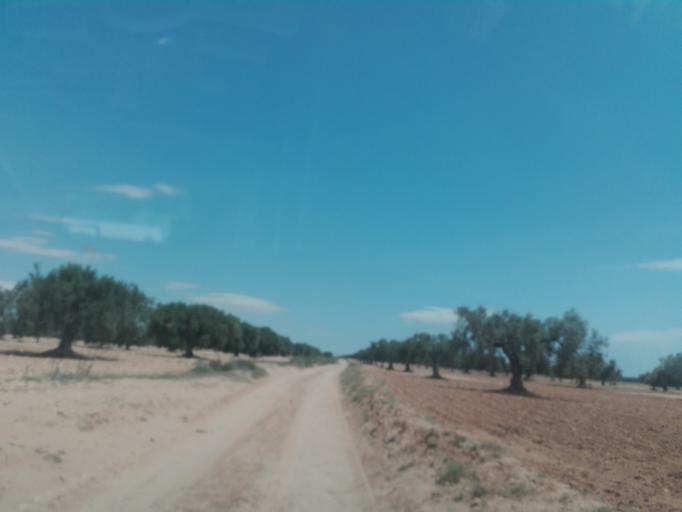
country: TN
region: Safaqis
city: Sfax
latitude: 34.6560
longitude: 10.5961
